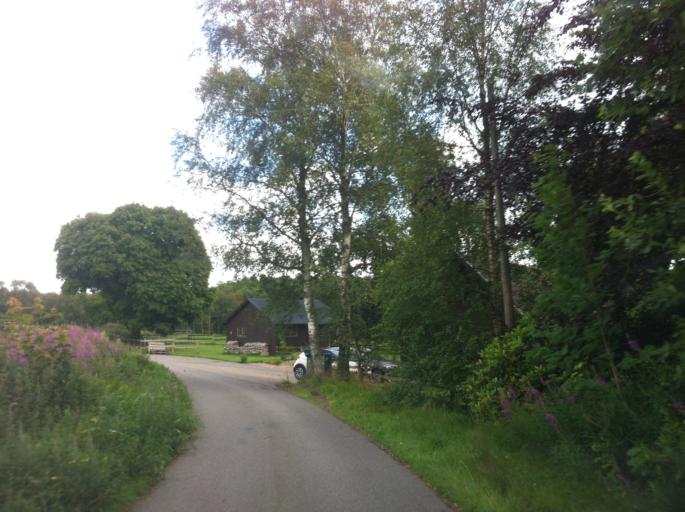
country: SE
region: Skane
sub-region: Bastads Kommun
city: Bastad
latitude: 56.4163
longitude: 12.9215
